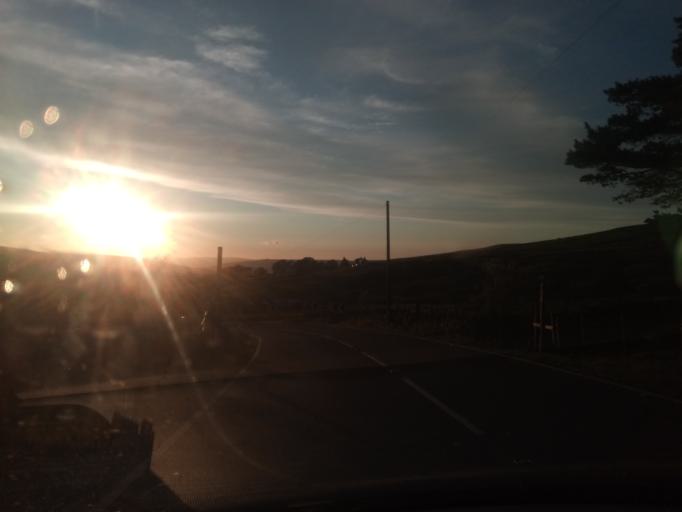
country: GB
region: England
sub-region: Northumberland
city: Bardon Mill
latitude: 54.7872
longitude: -2.3346
